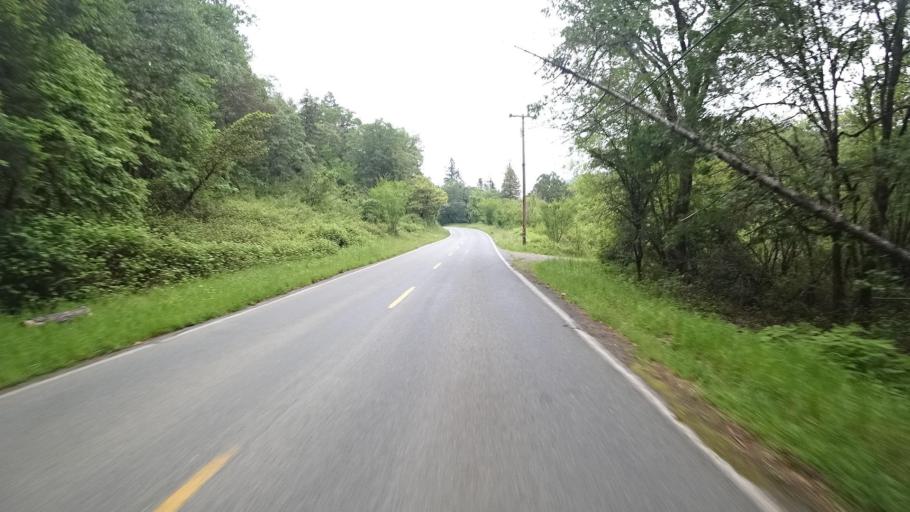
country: US
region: California
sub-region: Humboldt County
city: Willow Creek
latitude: 41.0692
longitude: -123.6943
